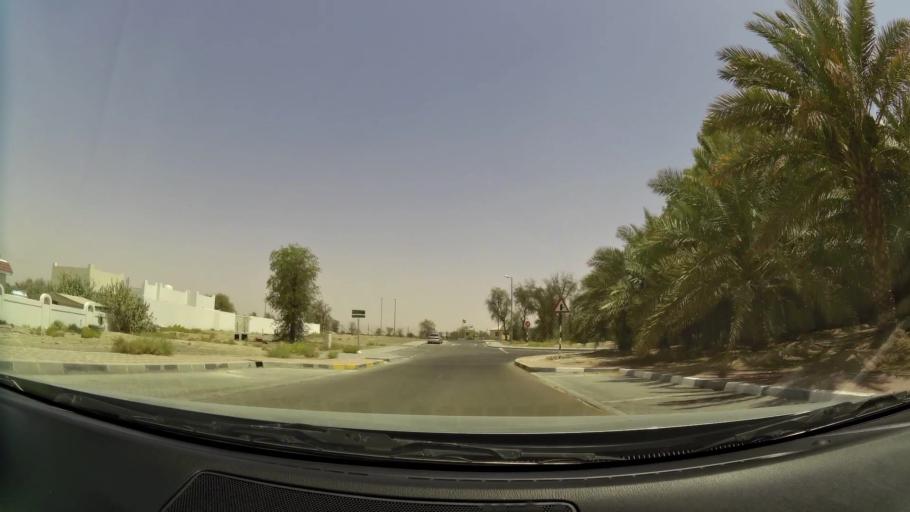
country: OM
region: Al Buraimi
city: Al Buraymi
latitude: 24.2777
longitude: 55.7477
